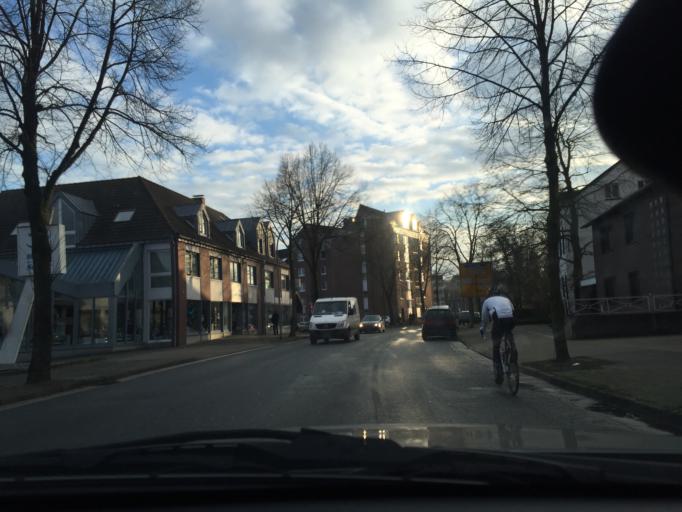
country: DE
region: North Rhine-Westphalia
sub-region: Regierungsbezirk Dusseldorf
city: Kleve
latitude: 51.7846
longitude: 6.1307
